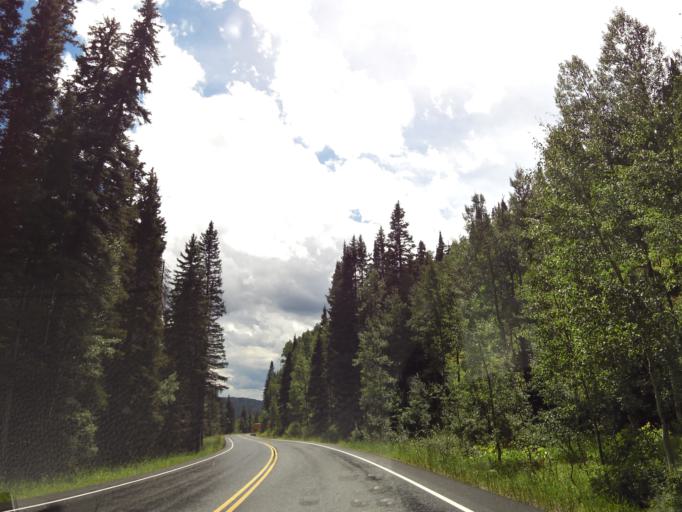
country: US
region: Colorado
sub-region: San Juan County
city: Silverton
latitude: 37.6715
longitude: -107.7957
